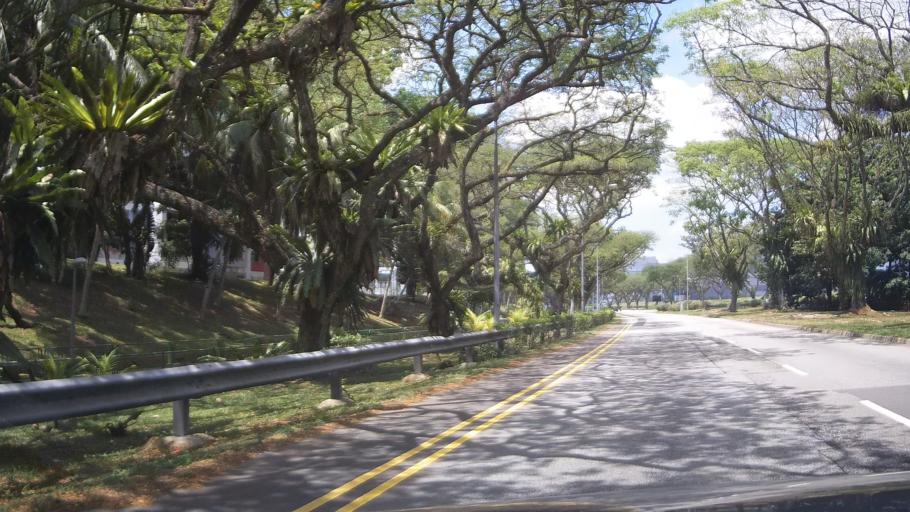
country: MY
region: Johor
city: Johor Bahru
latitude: 1.3549
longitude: 103.7180
